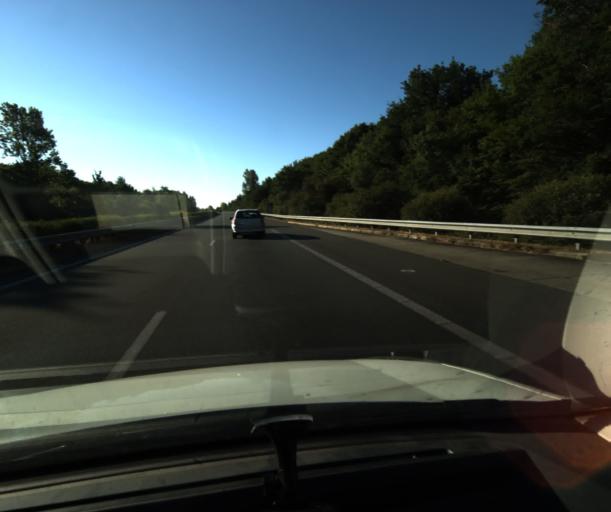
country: FR
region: Midi-Pyrenees
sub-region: Departement du Tarn-et-Garonne
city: Montech
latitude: 43.9902
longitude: 1.2359
